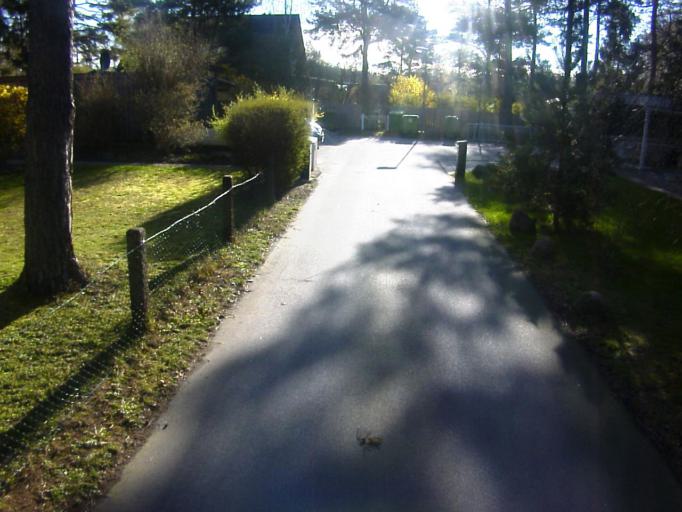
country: SE
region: Skane
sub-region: Kavlinge Kommun
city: Hofterup
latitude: 55.8006
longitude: 12.9763
